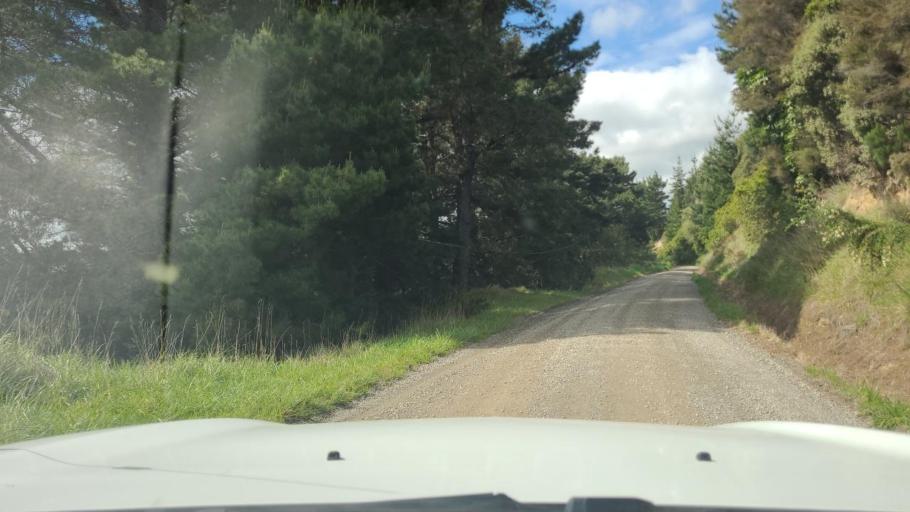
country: NZ
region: Wellington
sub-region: South Wairarapa District
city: Waipawa
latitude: -41.2150
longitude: 175.5774
